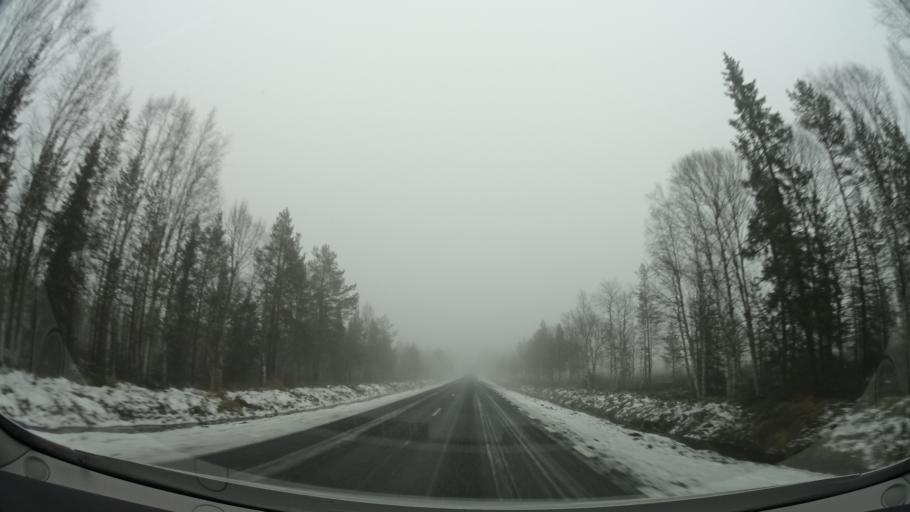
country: SE
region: Vaesterbotten
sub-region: Asele Kommun
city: Insjon
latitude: 64.2903
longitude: 17.6527
